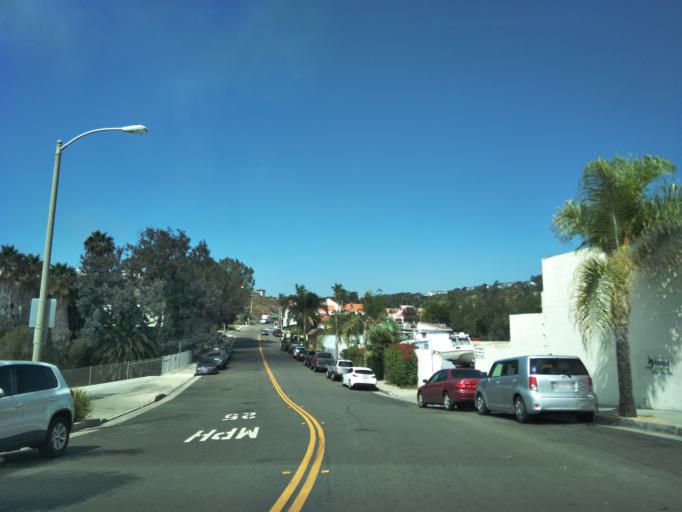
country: US
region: California
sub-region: Orange County
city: San Clemente
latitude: 33.4353
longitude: -117.6244
